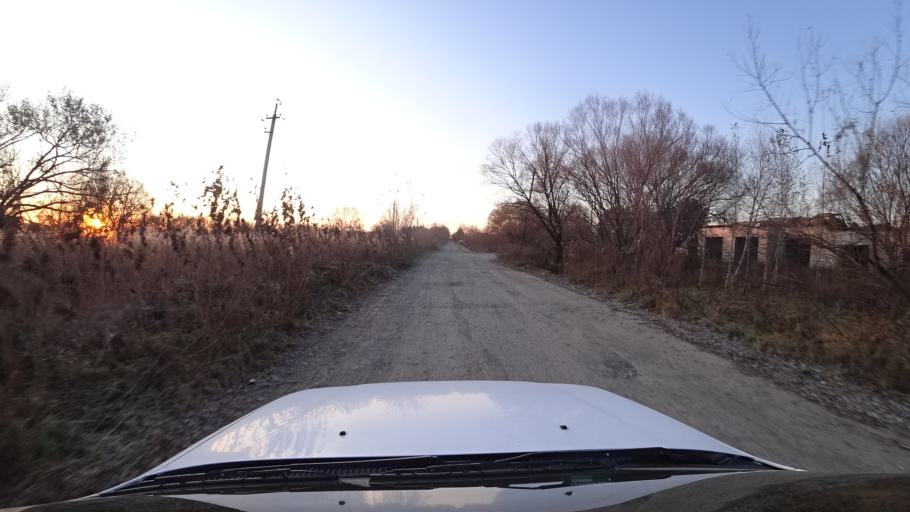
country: RU
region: Primorskiy
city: Dal'nerechensk
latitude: 45.9195
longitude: 133.7372
